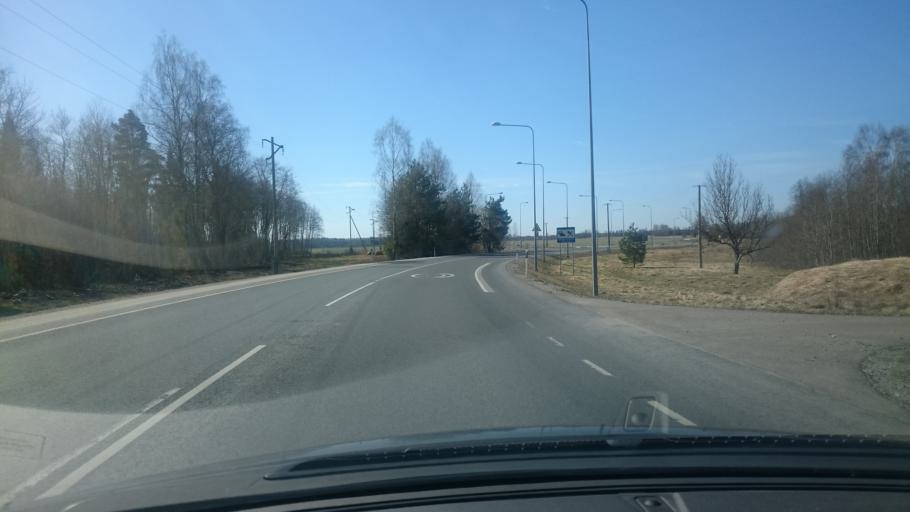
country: EE
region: Raplamaa
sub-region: Rapla vald
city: Rapla
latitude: 59.0428
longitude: 24.8394
